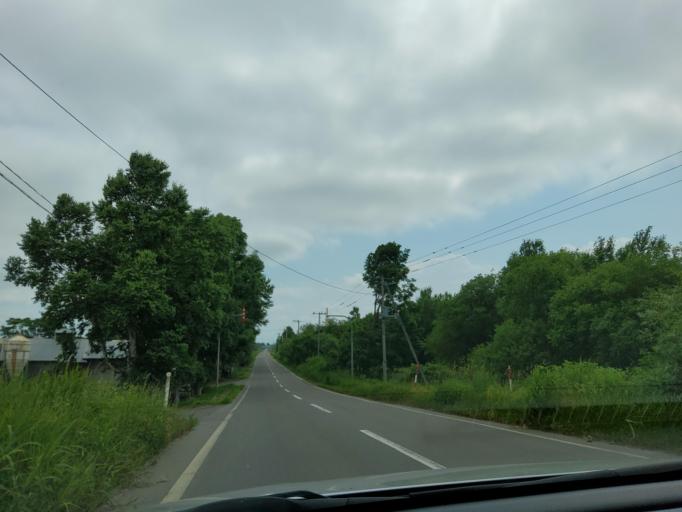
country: JP
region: Hokkaido
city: Obihiro
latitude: 42.8977
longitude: 143.1212
